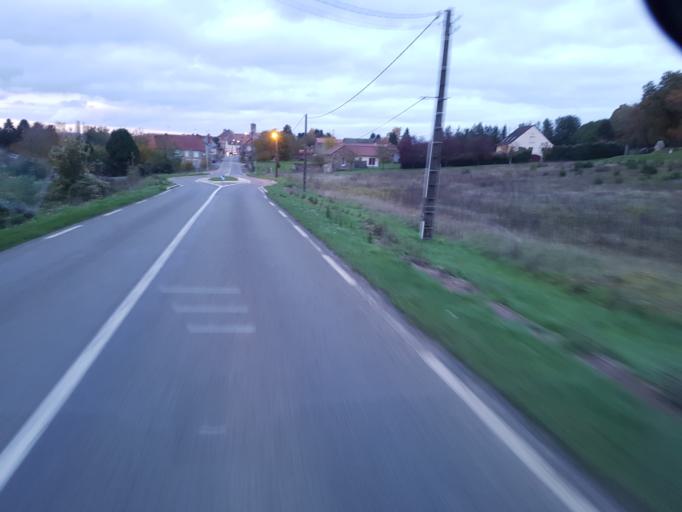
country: FR
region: Picardie
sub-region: Departement de l'Aisne
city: Coincy
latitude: 49.1478
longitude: 3.3874
